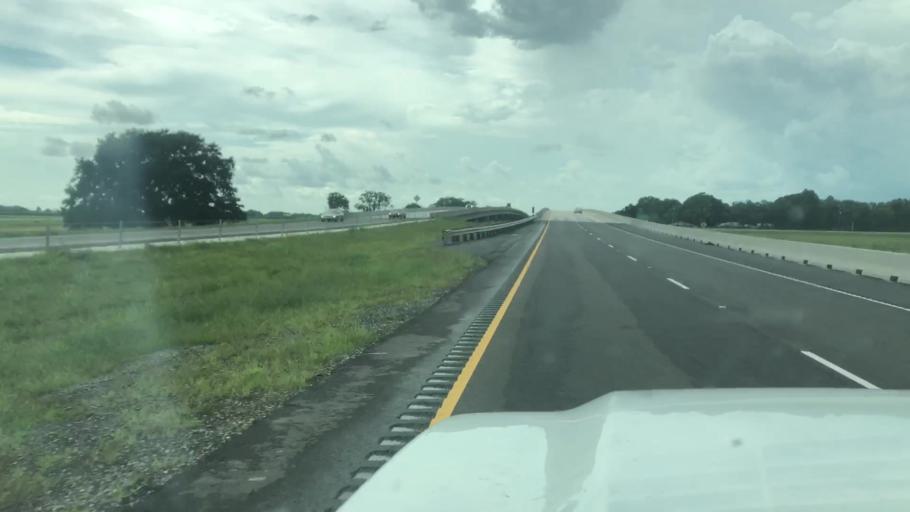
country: US
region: Louisiana
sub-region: Iberia Parish
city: Jeanerette
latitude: 29.8648
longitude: -91.6299
